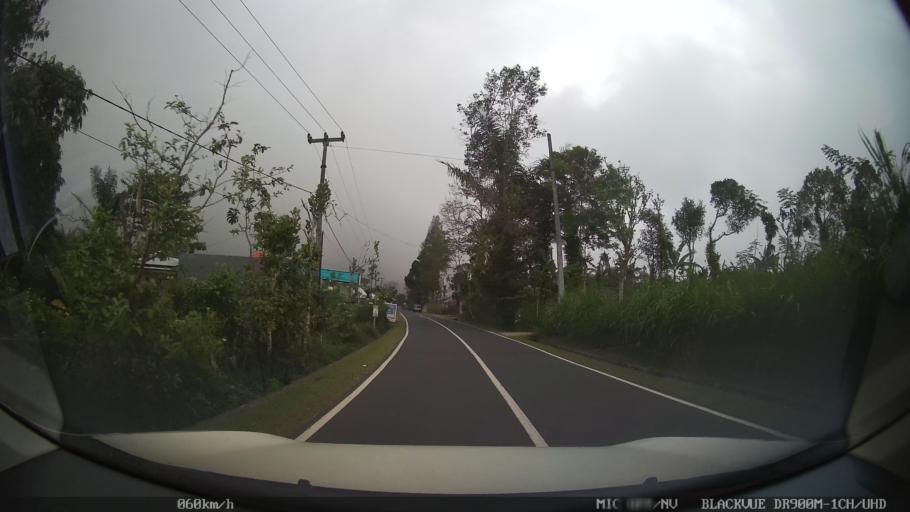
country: ID
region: Bali
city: Banjar Kedisan
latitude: -8.2835
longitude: 115.3207
